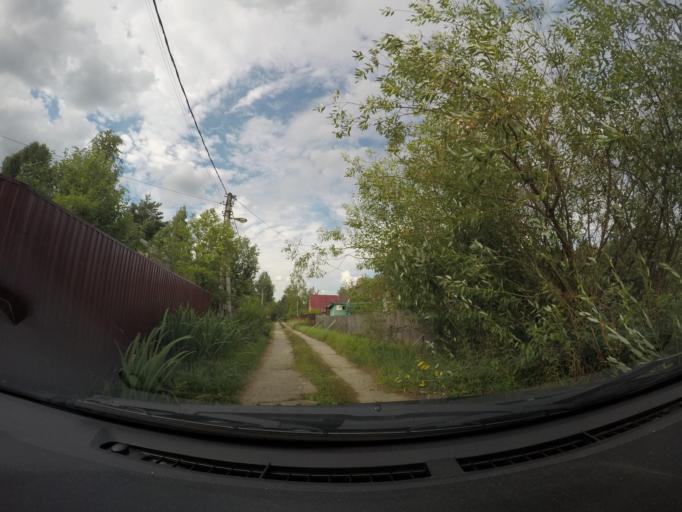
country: RU
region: Moskovskaya
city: Rechitsy
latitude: 55.6087
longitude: 38.4983
